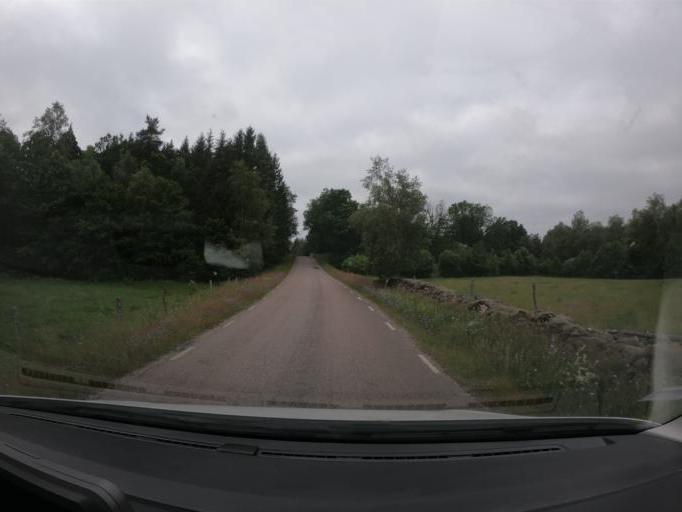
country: SE
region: Skane
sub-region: Perstorps Kommun
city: Perstorp
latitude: 56.1097
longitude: 13.3529
